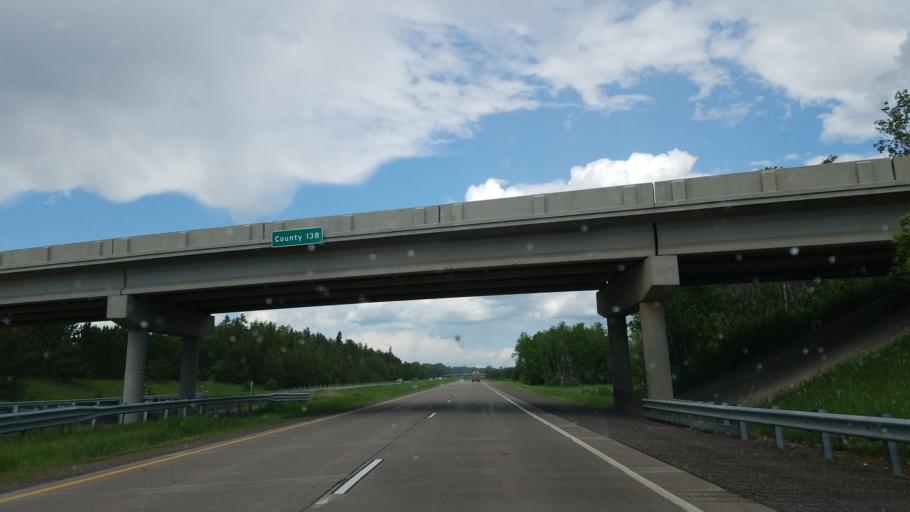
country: US
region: Minnesota
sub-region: Carlton County
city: Moose Lake
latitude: 46.4902
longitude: -92.6992
